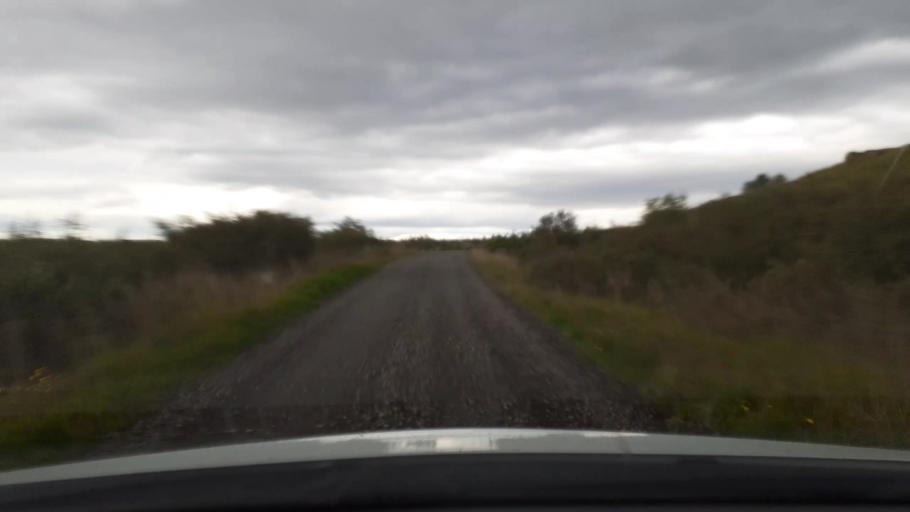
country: IS
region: West
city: Borgarnes
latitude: 64.6398
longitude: -21.7518
